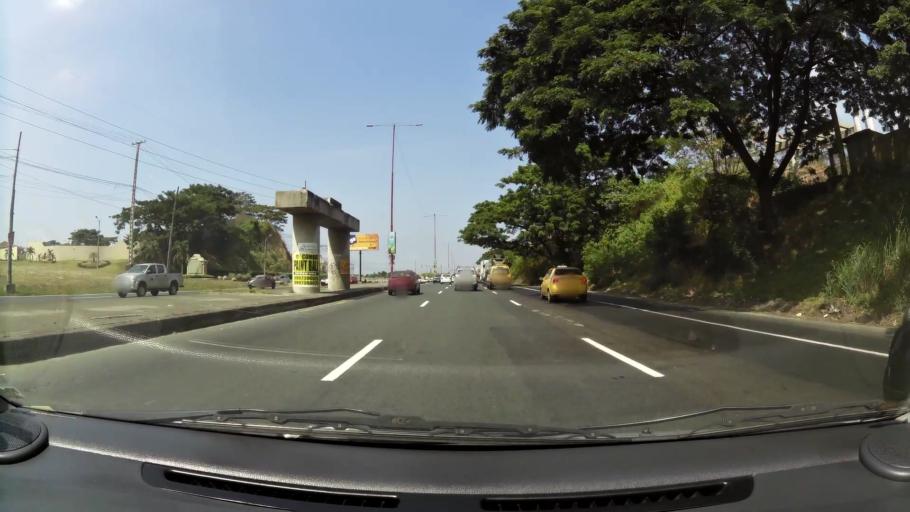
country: EC
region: Guayas
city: El Triunfo
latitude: -2.0493
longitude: -79.9056
